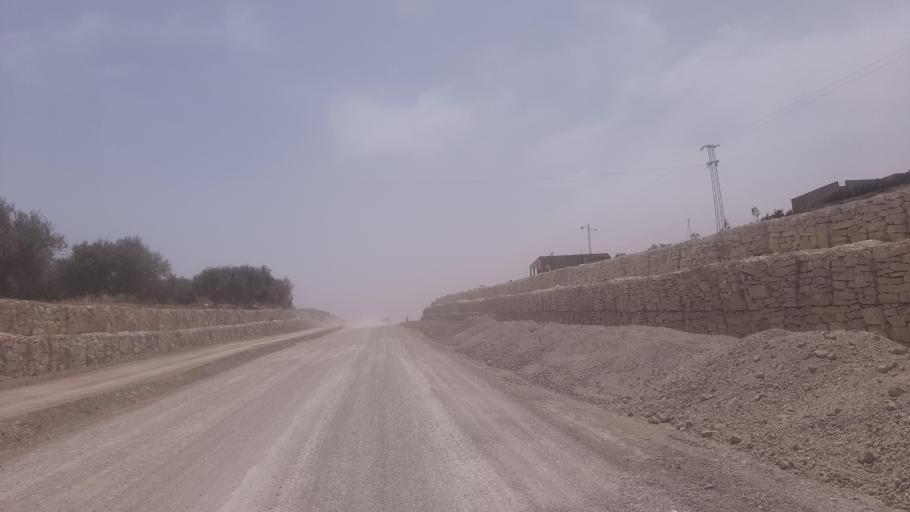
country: TN
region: Zaghwan
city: Zaghouan
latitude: 36.5318
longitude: 10.1570
